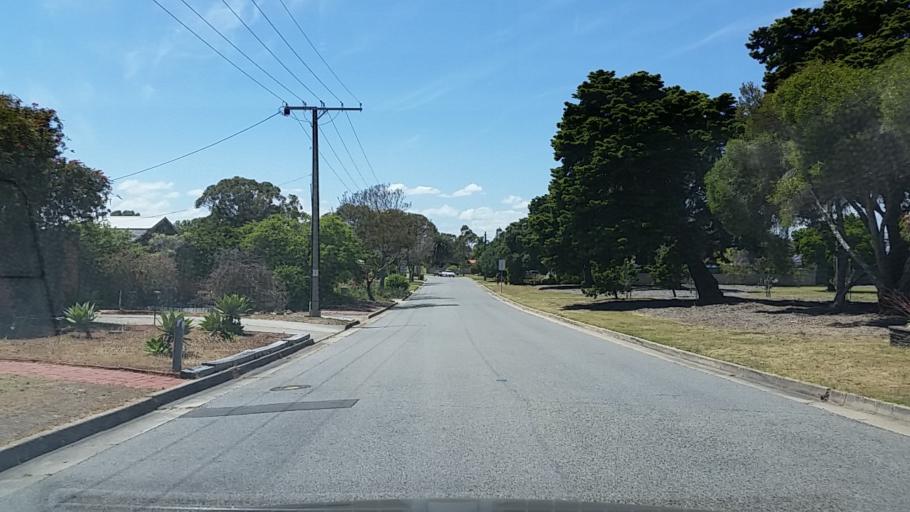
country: AU
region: South Australia
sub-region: Charles Sturt
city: Grange
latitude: -34.8892
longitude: 138.4990
